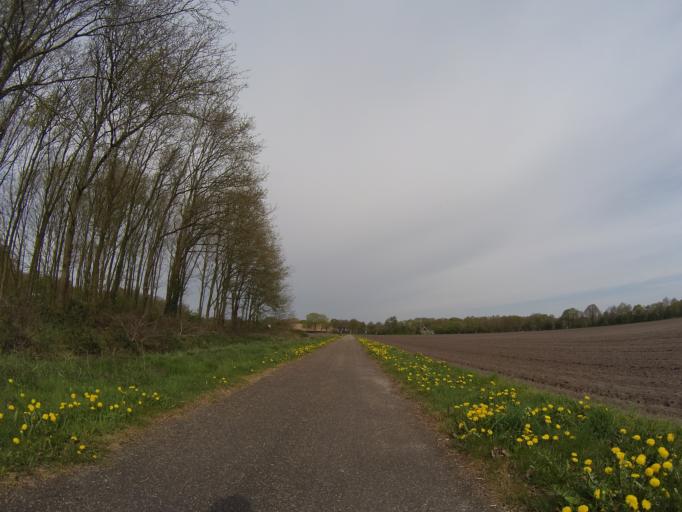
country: NL
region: Drenthe
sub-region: Gemeente Borger-Odoorn
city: Borger
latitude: 52.8400
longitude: 6.6649
